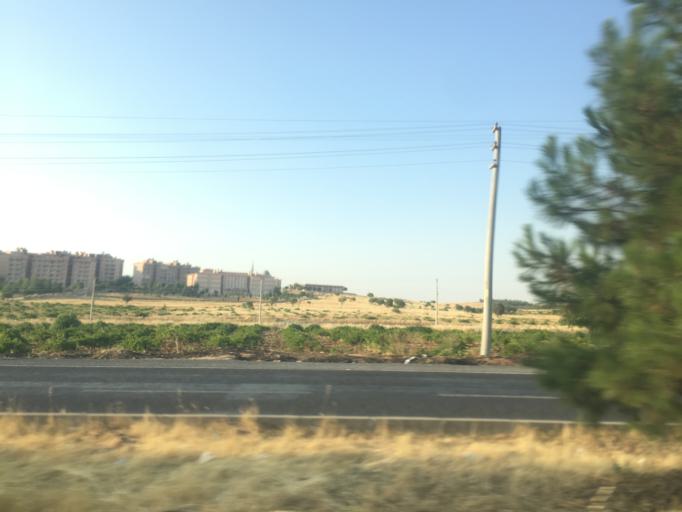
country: TR
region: Mardin
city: Midyat
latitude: 37.4365
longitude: 41.3174
